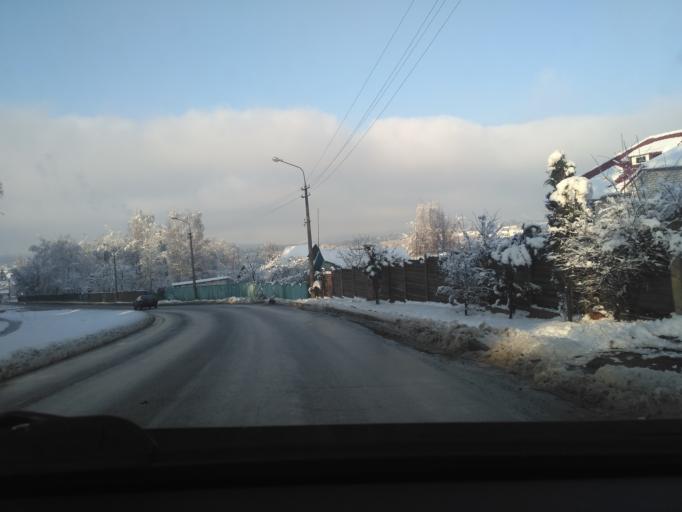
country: BY
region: Minsk
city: Horad Barysaw
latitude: 54.2328
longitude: 28.5003
